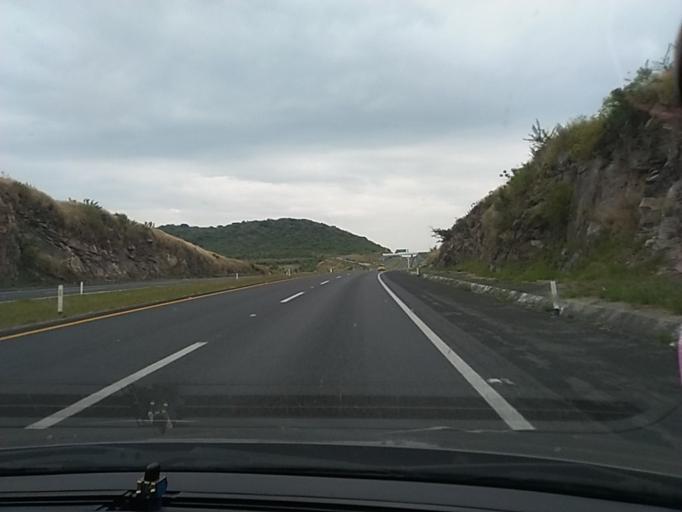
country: MX
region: Michoacan
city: Penjamillo de Degollado
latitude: 20.0439
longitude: -101.9393
